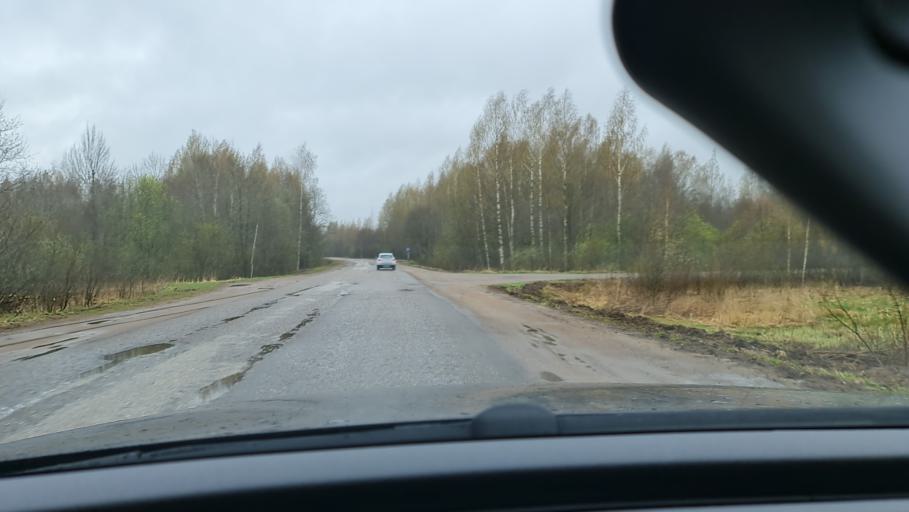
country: RU
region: Novgorod
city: Kresttsy
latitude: 57.9670
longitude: 32.7114
